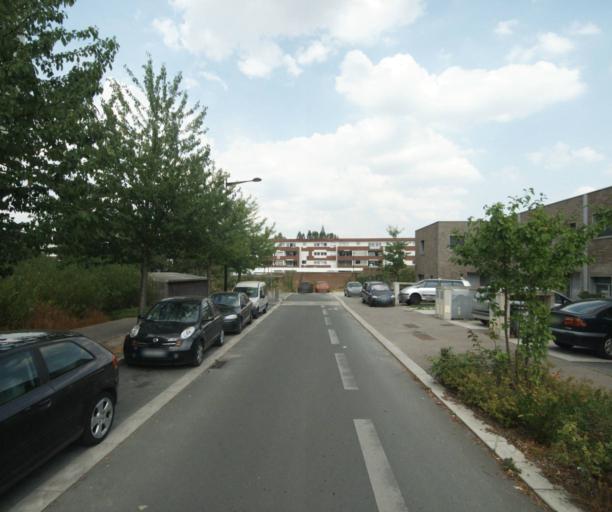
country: FR
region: Nord-Pas-de-Calais
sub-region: Departement du Nord
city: Tourcoing
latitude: 50.7301
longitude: 3.1467
